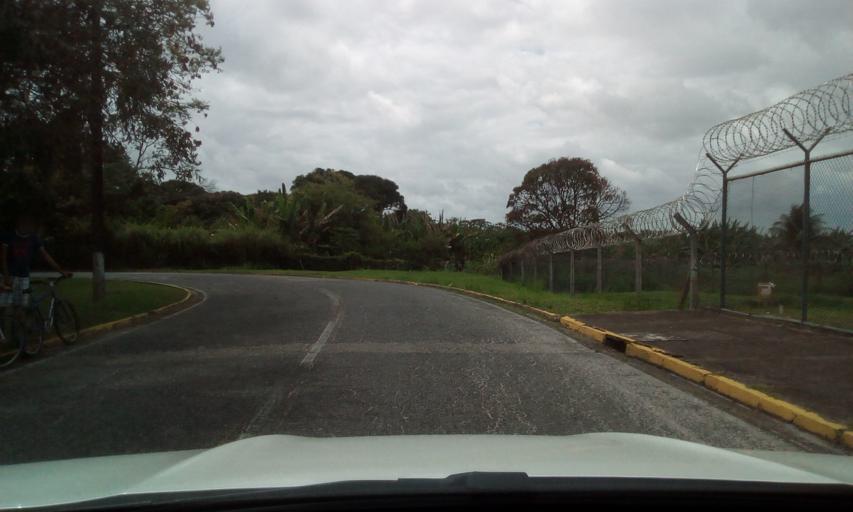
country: BR
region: Paraiba
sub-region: Bayeux
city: Bayeux
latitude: -7.1465
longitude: -34.9476
